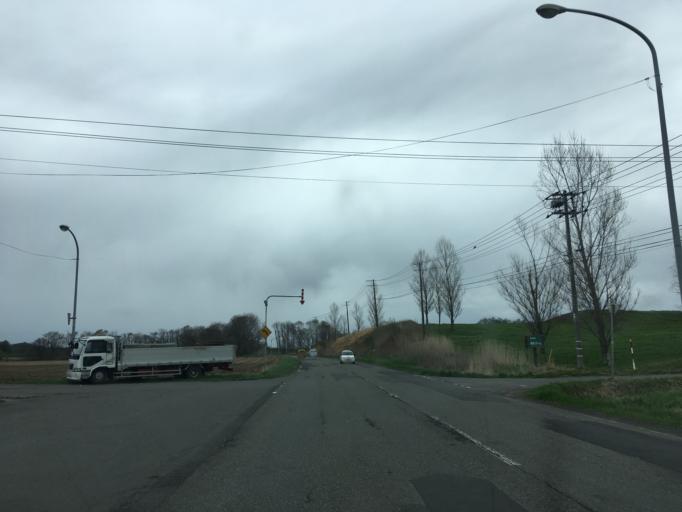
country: JP
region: Hokkaido
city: Chitose
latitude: 42.8971
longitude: 141.8137
